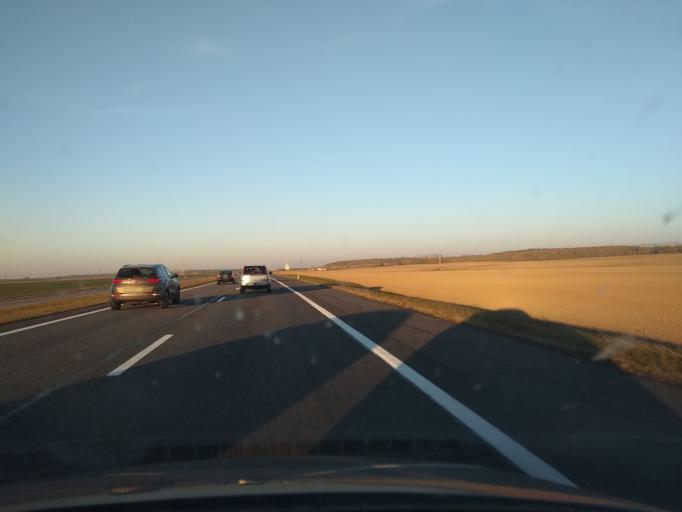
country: BY
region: Brest
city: Baranovichi
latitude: 53.2235
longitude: 26.1569
